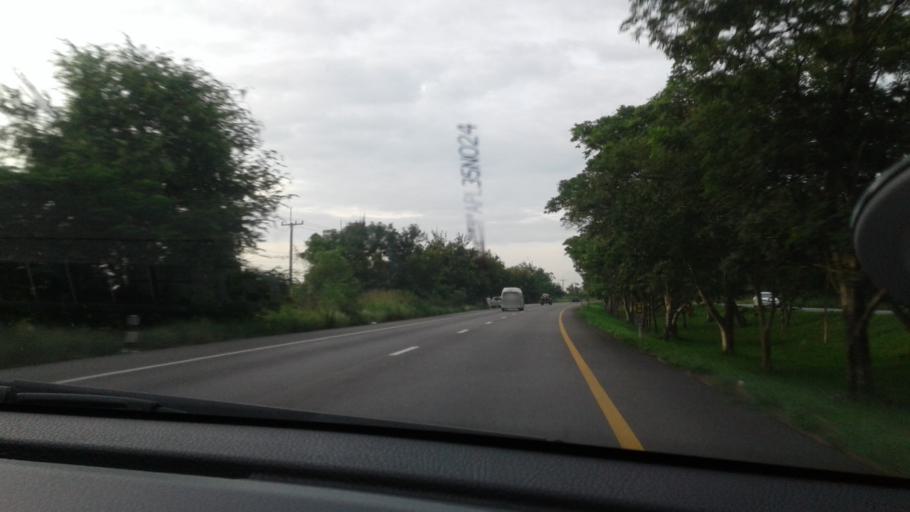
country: TH
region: Prachuap Khiri Khan
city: Pran Buri
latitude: 12.4595
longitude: 99.8987
